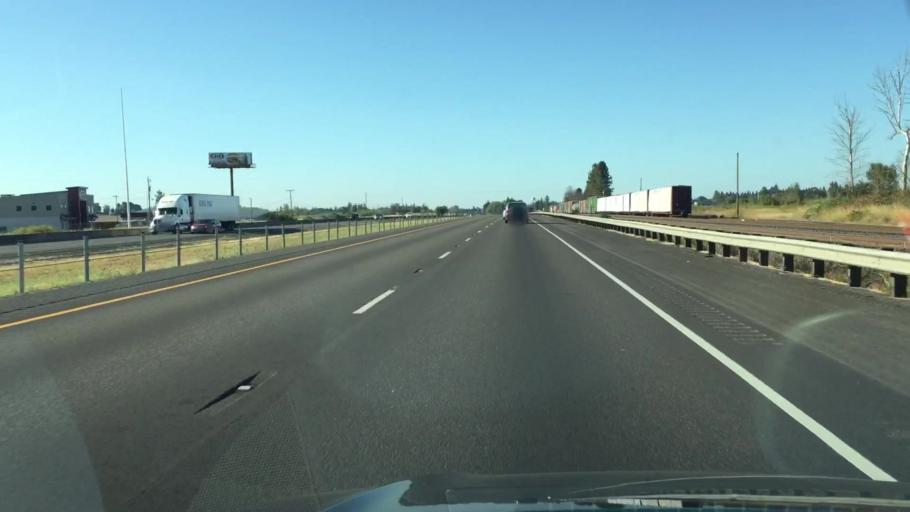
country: US
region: Oregon
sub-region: Linn County
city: Millersburg
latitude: 44.6805
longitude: -123.0551
